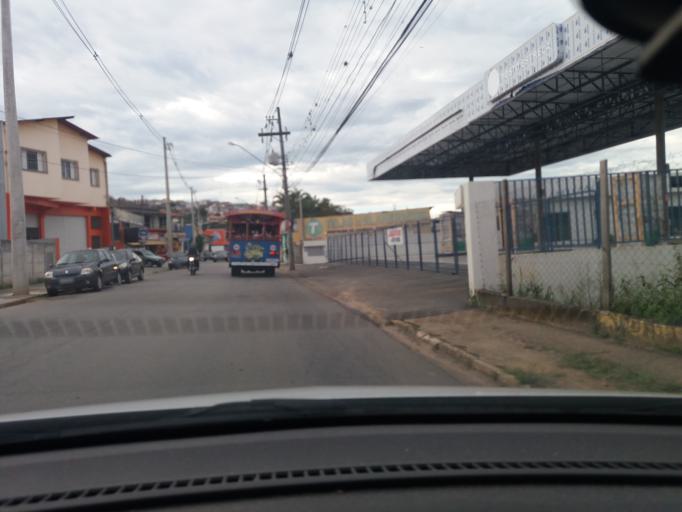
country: BR
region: Sao Paulo
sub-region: Bom Jesus Dos Perdoes
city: Bom Jesus dos Perdoes
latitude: -23.1279
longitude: -46.4679
